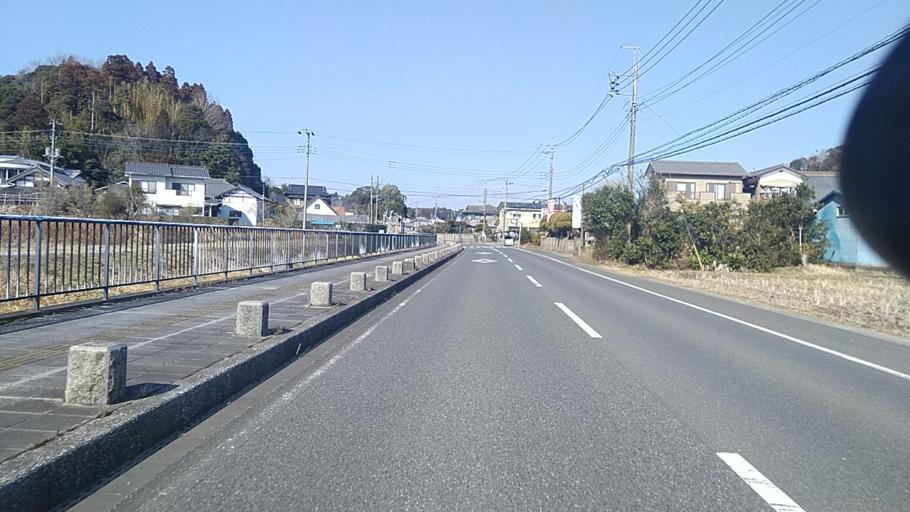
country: JP
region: Chiba
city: Oami
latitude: 35.4765
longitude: 140.2808
